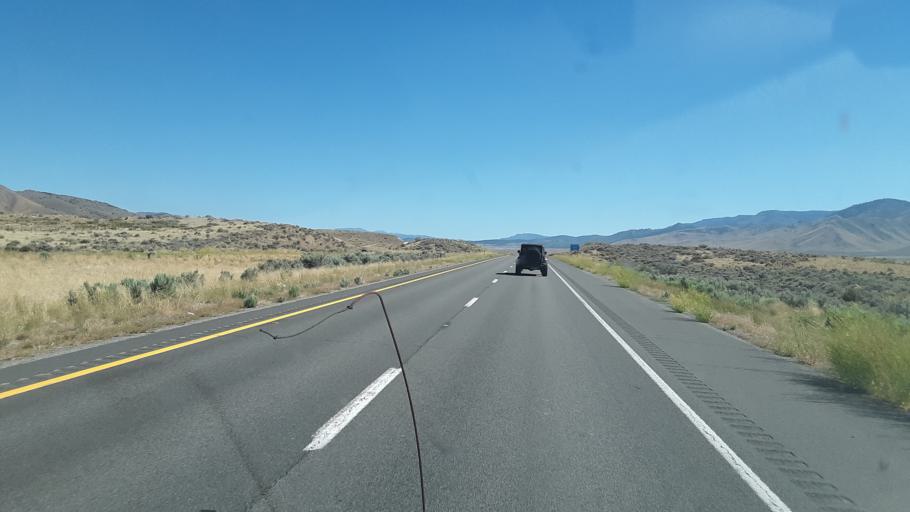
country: US
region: Nevada
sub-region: Washoe County
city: Cold Springs
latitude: 39.7535
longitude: -120.0395
